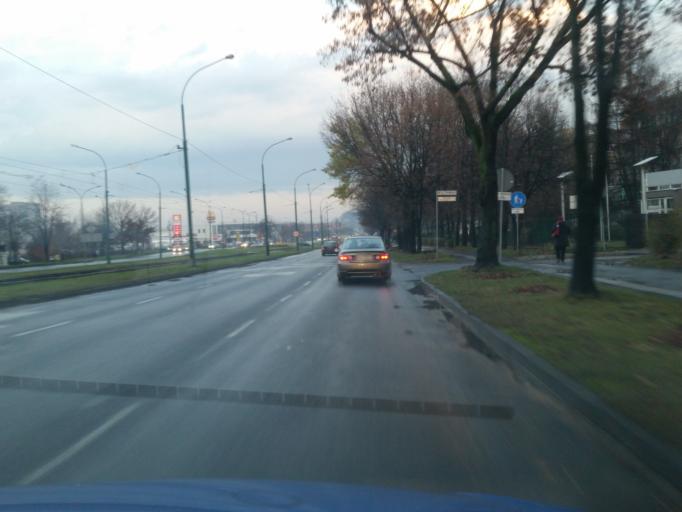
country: PL
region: Silesian Voivodeship
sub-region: Dabrowa Gornicza
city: Dabrowa Gornicza
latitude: 50.3290
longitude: 19.2126
